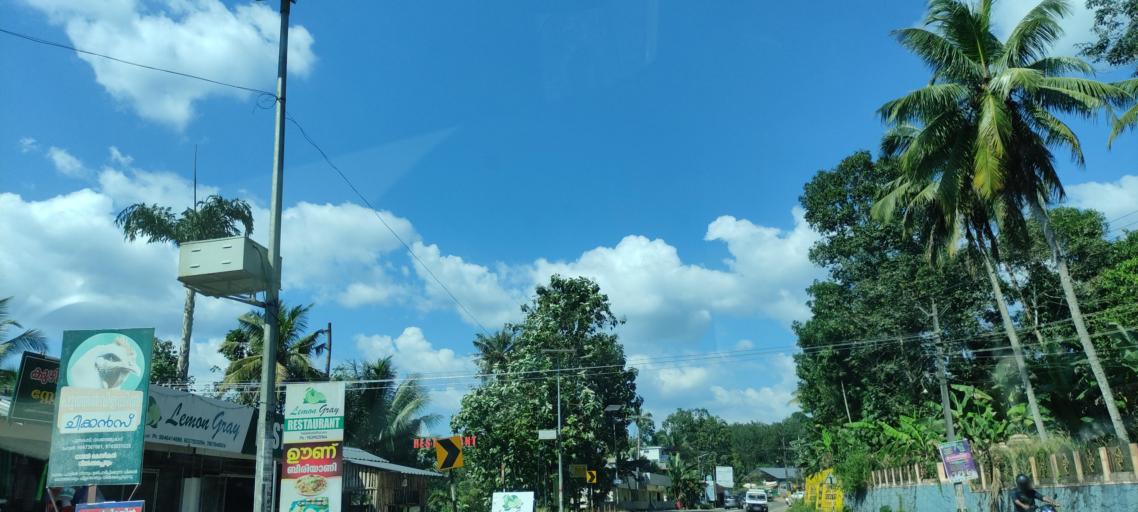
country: IN
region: Kerala
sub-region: Pattanamtitta
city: Adur
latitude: 9.1355
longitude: 76.7355
